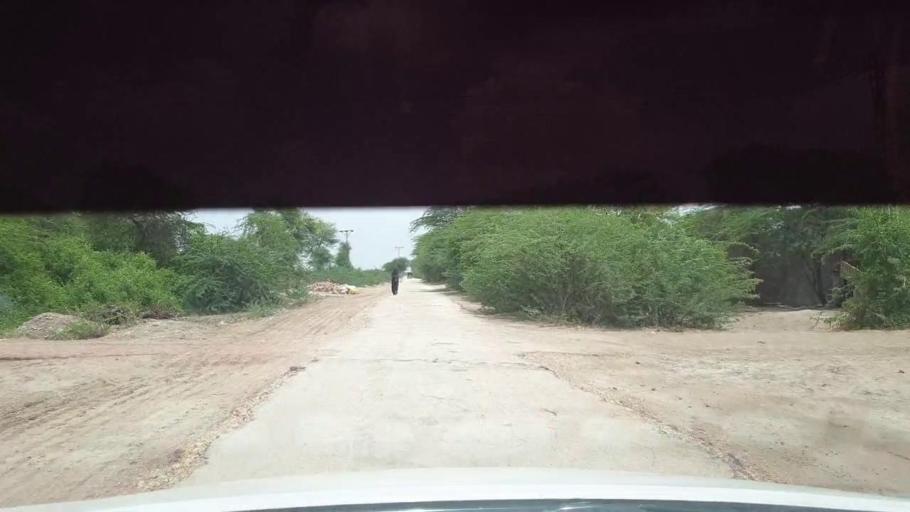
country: PK
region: Sindh
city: Kadhan
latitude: 24.4651
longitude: 69.0136
